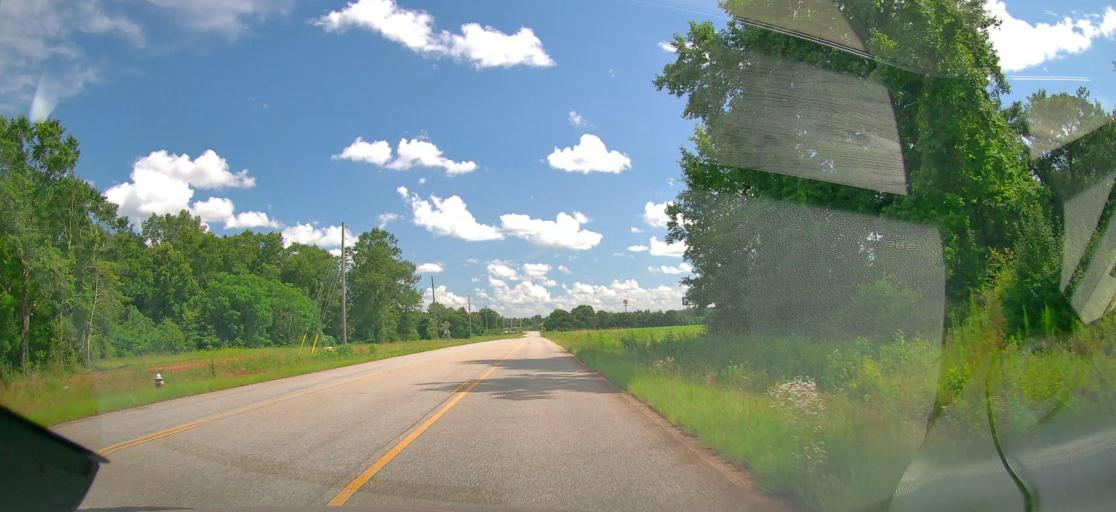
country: US
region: Georgia
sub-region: Houston County
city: Centerville
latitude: 32.5946
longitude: -83.7392
